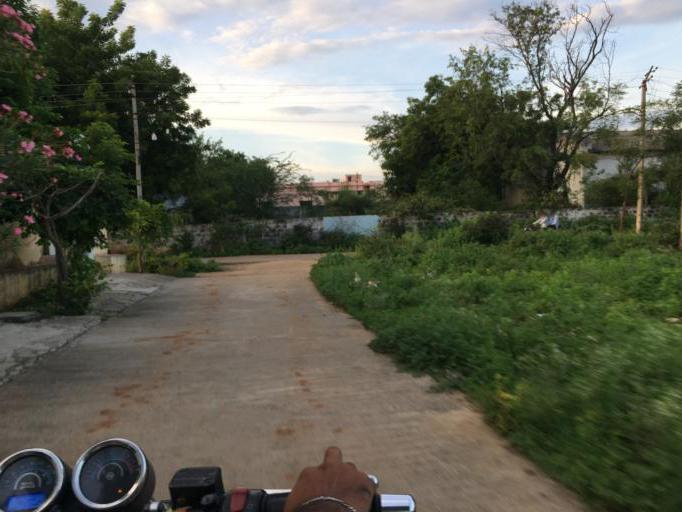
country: IN
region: Telangana
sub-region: Nalgonda
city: Nalgonda
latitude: 17.1739
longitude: 79.4179
